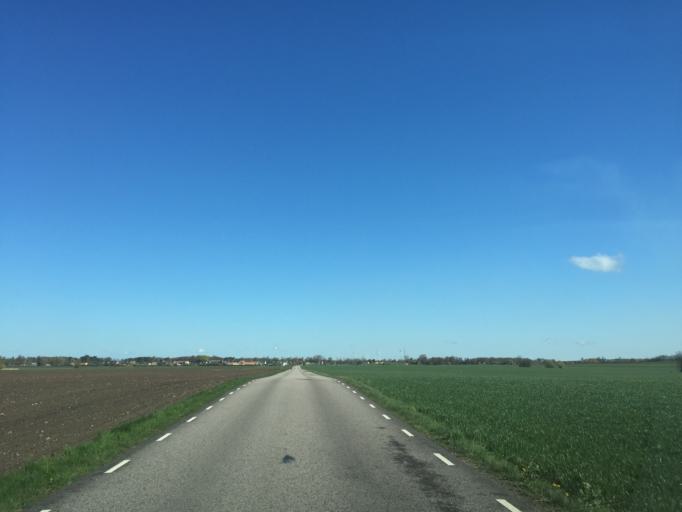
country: SE
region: Skane
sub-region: Kavlinge Kommun
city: Loddekopinge
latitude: 55.8085
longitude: 13.0253
